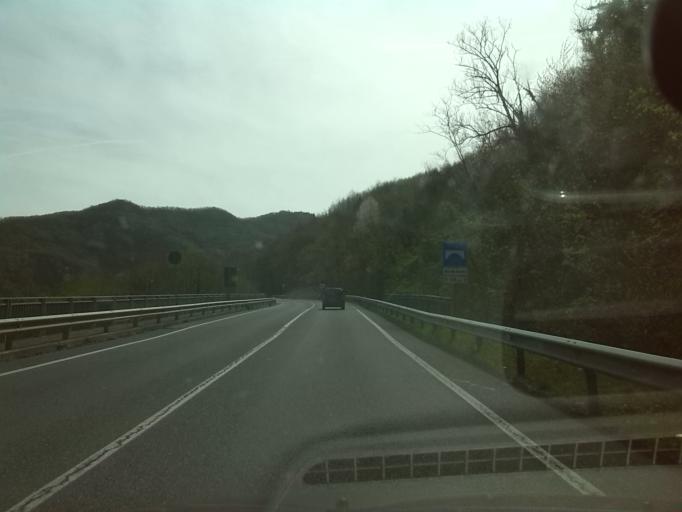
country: IT
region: Liguria
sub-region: Provincia di Imperia
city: Pieve di Teco
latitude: 44.0371
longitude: 7.9346
